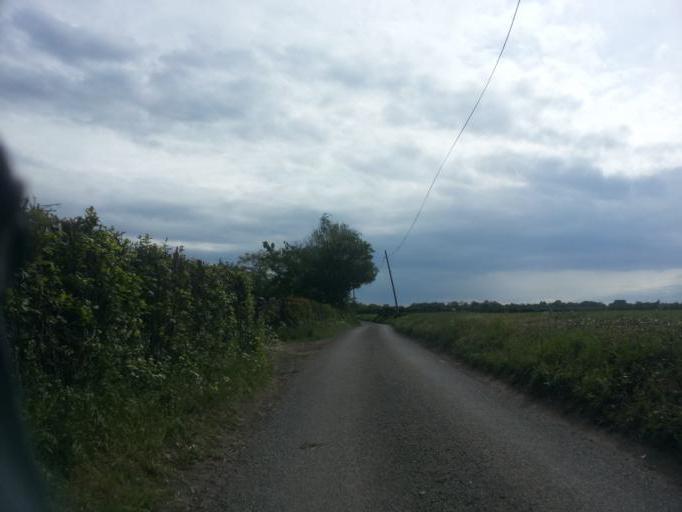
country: GB
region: England
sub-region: Kent
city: Teynham
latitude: 51.3267
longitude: 0.8407
